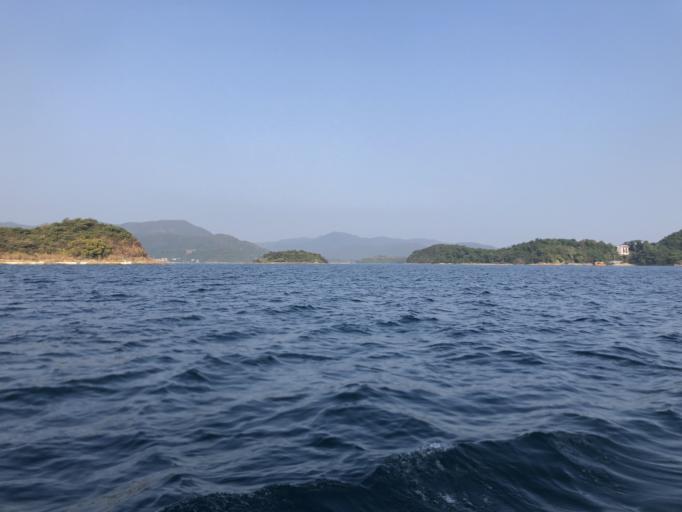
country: HK
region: Sai Kung
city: Sai Kung
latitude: 22.3715
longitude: 114.2840
